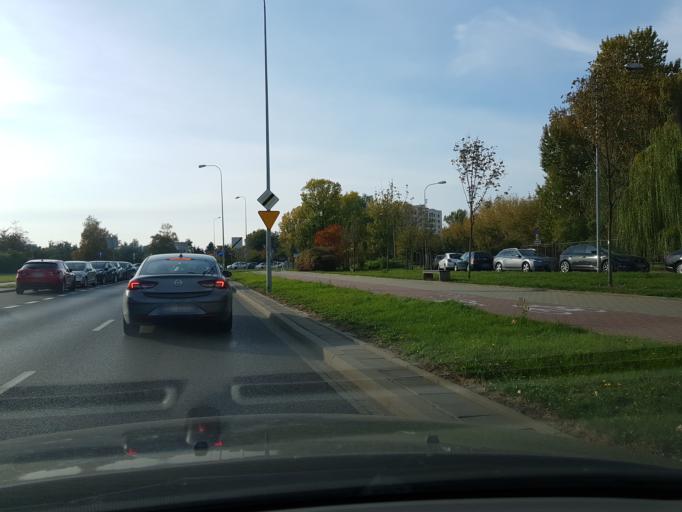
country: PL
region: Masovian Voivodeship
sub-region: Warszawa
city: Mokotow
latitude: 52.1956
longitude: 21.0427
